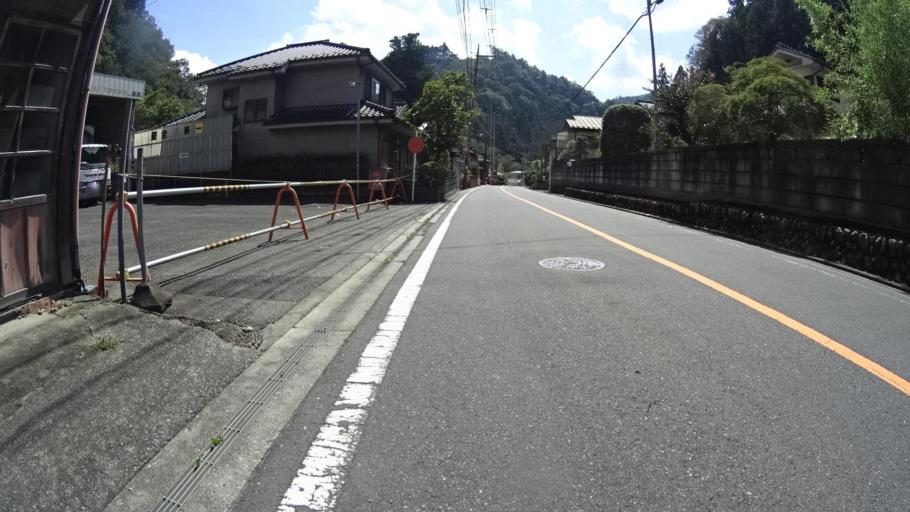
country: JP
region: Tokyo
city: Itsukaichi
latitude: 35.7281
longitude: 139.1462
